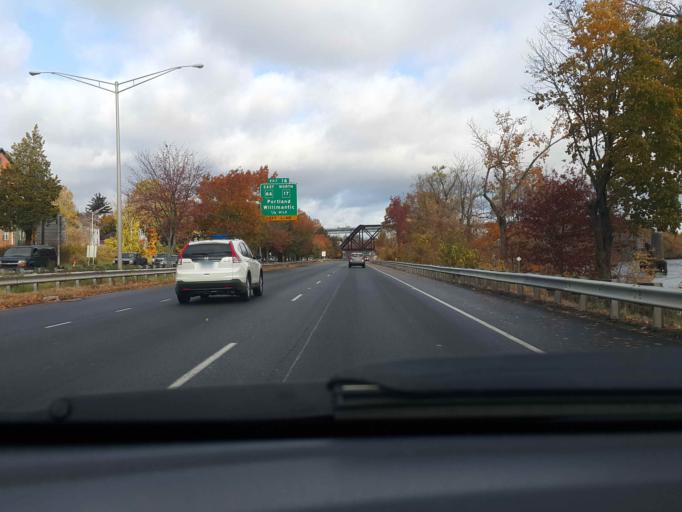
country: US
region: Connecticut
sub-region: Middlesex County
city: Middletown
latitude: 41.5638
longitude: -72.6482
